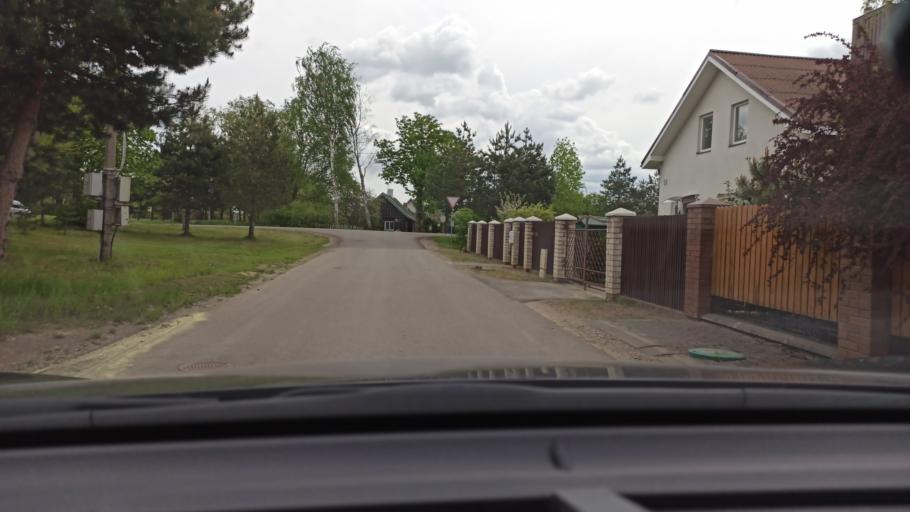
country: LT
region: Siauliu apskritis
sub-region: Siauliai
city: Siauliai
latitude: 55.9033
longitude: 23.3323
